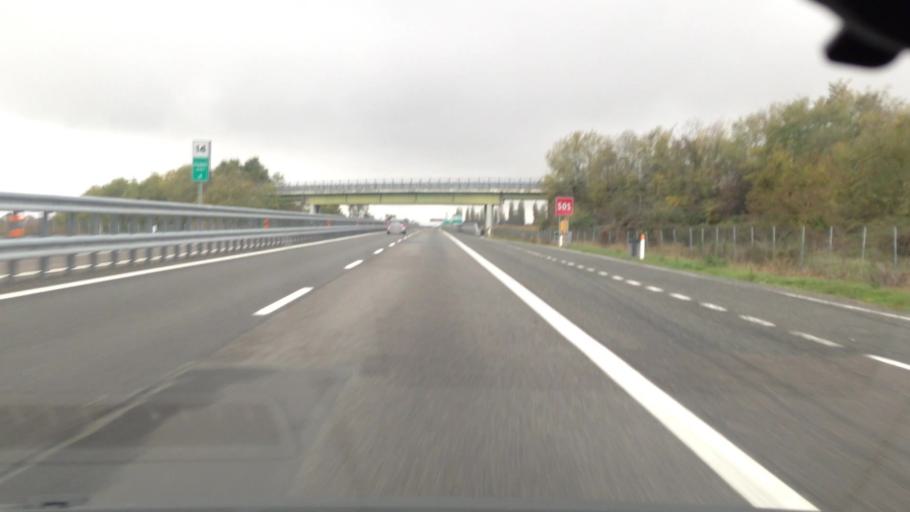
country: IT
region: Piedmont
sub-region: Provincia di Asti
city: San Paolo Solbrito
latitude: 44.9487
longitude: 7.9632
